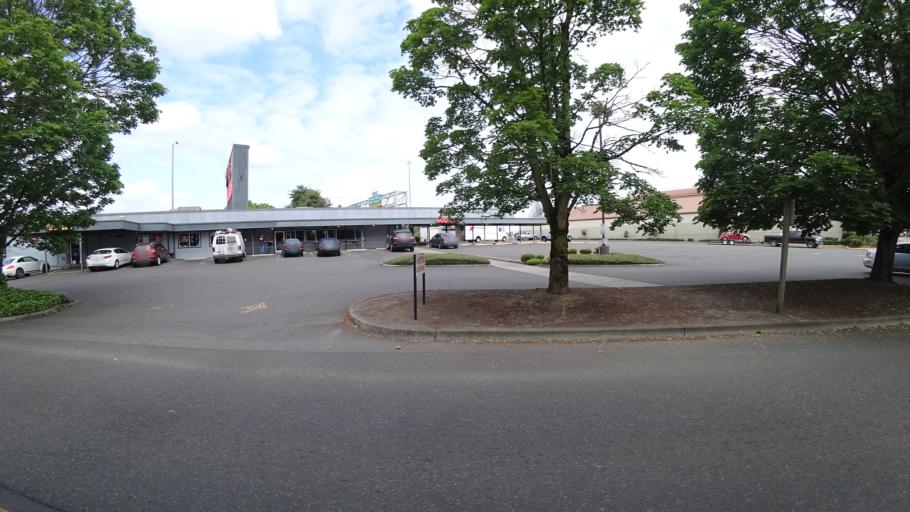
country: US
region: Washington
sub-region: Clark County
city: Vancouver
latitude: 45.6091
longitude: -122.6793
